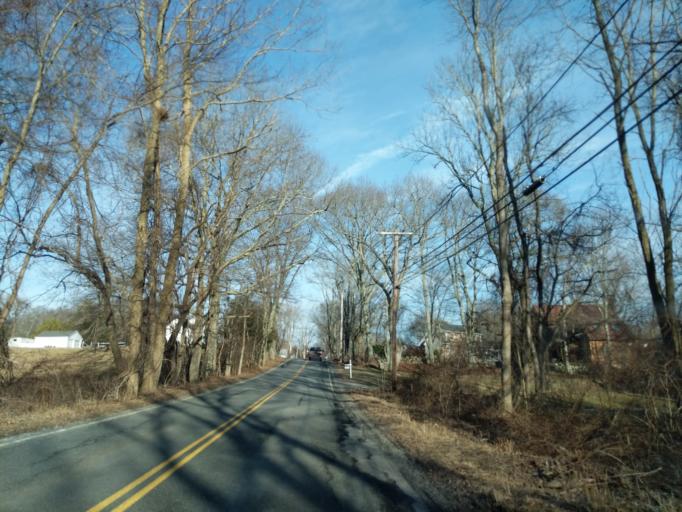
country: US
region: Massachusetts
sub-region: Worcester County
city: Blackstone
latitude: 42.0260
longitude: -71.5547
